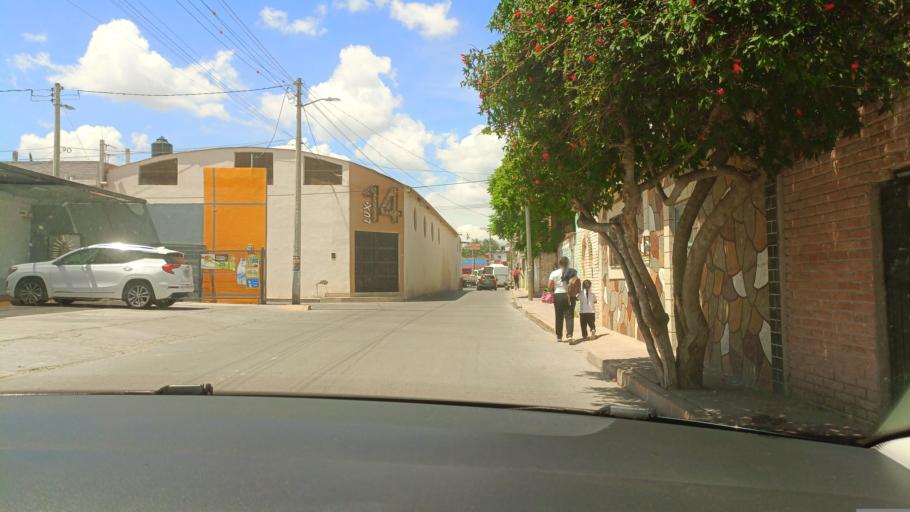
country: MX
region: Guanajuato
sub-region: San Luis de la Paz
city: San Luis de la Paz
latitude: 21.3026
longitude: -100.5217
